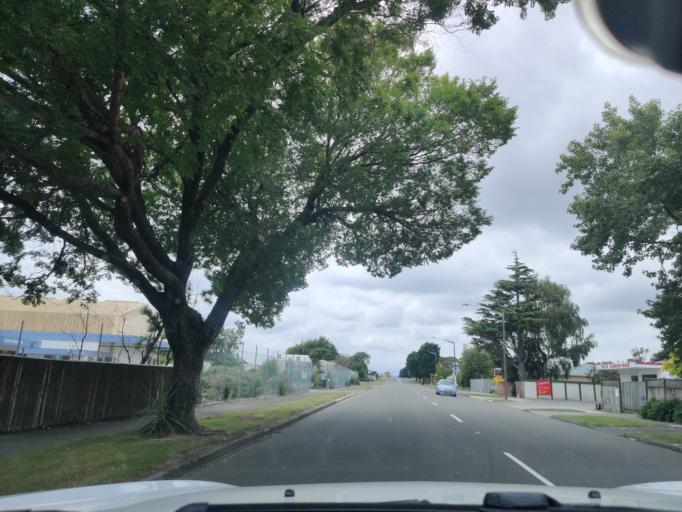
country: NZ
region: Manawatu-Wanganui
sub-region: Palmerston North City
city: Palmerston North
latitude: -40.3499
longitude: 175.5871
